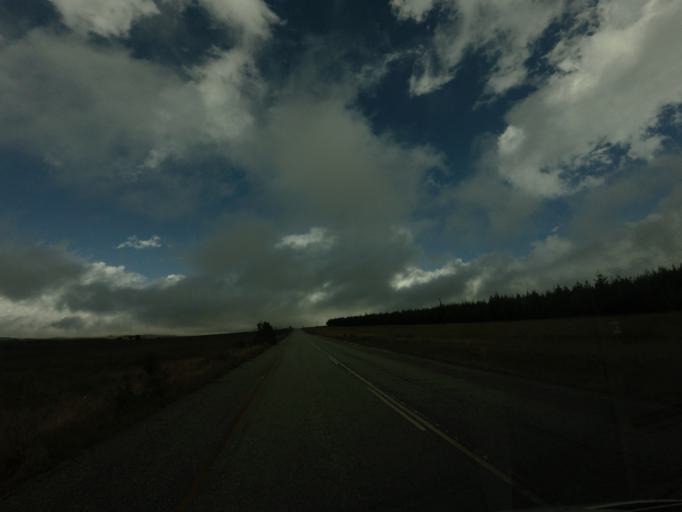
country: ZA
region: Mpumalanga
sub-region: Ehlanzeni District
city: Graksop
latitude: -24.8566
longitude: 30.8721
